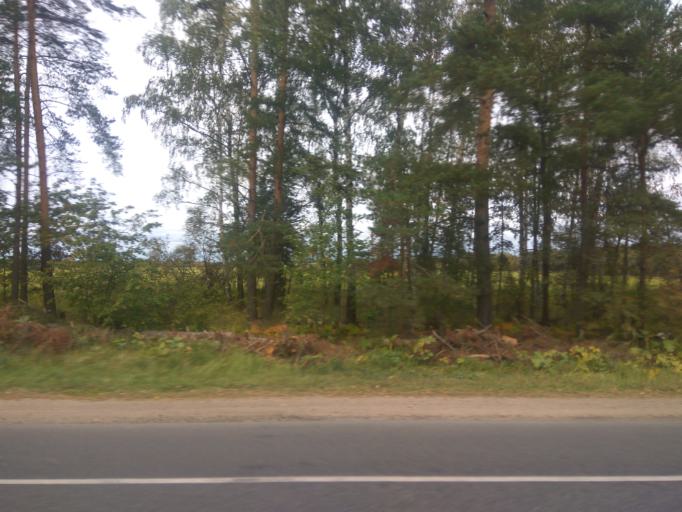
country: RU
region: Moskovskaya
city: Krasnoarmeysk
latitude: 56.0117
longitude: 38.1527
